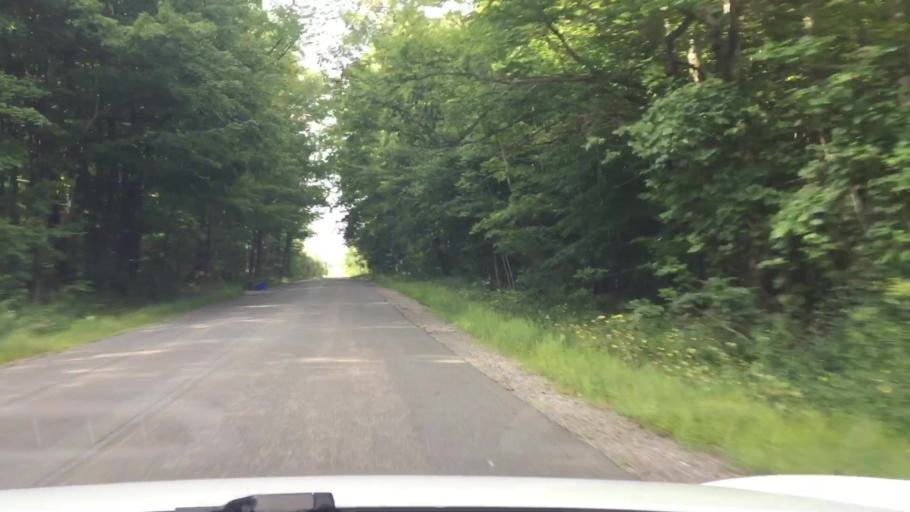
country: CA
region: Ontario
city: Oshawa
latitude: 43.9457
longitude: -78.7502
